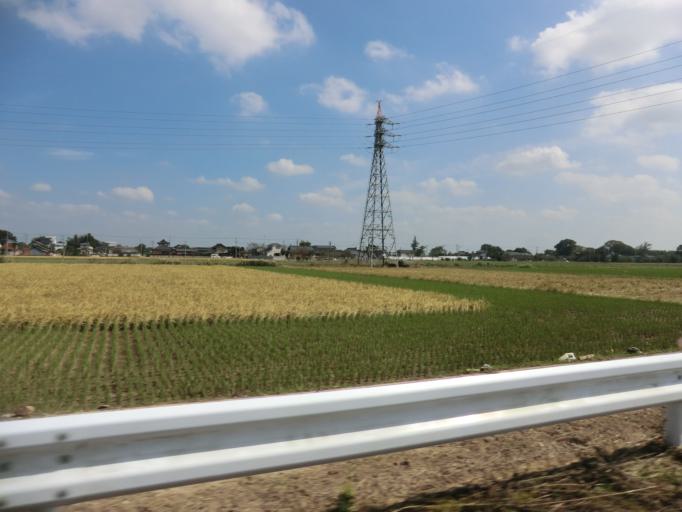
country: JP
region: Ibaraki
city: Mitsukaido
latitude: 36.0581
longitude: 139.9939
